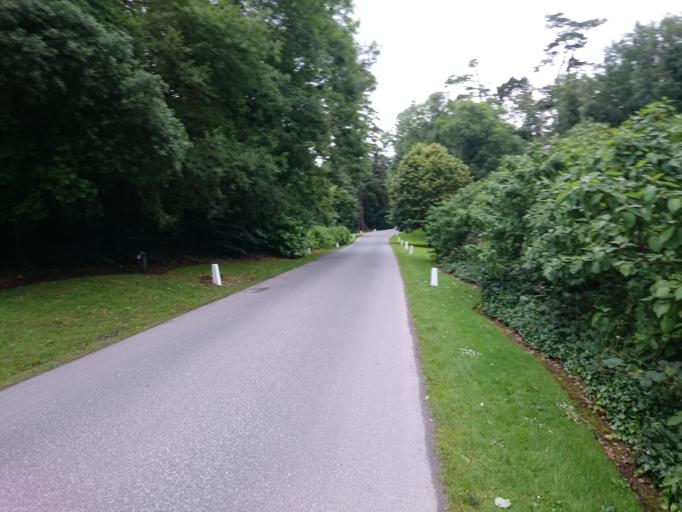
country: IE
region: Connaught
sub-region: Maigh Eo
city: Ballinrobe
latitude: 53.5374
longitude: -9.2850
